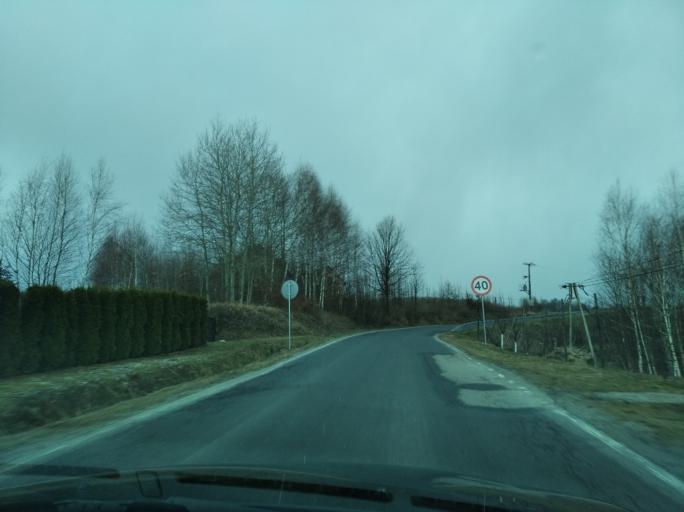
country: PL
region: Subcarpathian Voivodeship
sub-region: Powiat rzeszowski
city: Hyzne
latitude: 49.9161
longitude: 22.1983
